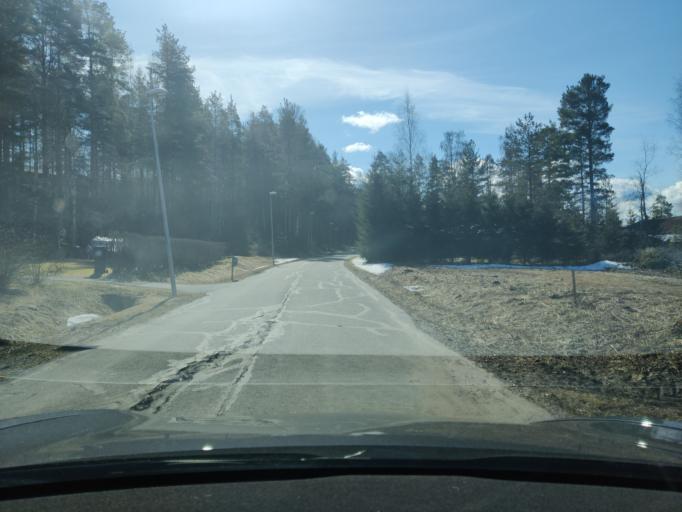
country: FI
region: Northern Savo
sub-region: Kuopio
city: Vehmersalmi
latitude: 62.7583
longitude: 28.0318
